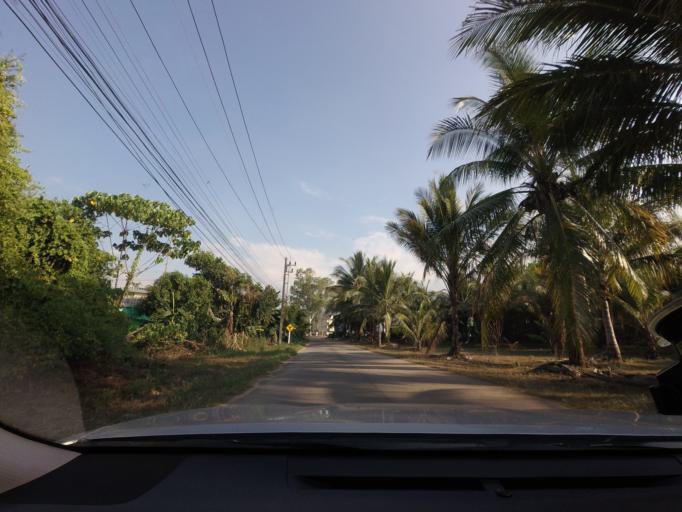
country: TH
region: Phangnga
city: Ban Khao Lak
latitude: 8.6893
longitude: 98.2520
